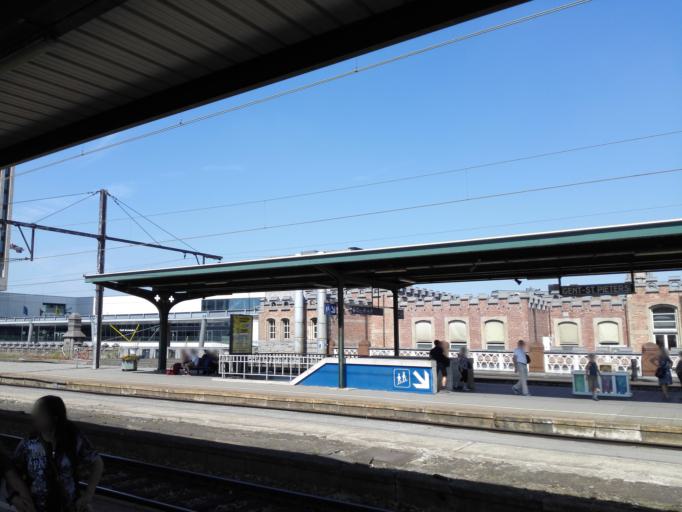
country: BE
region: Flanders
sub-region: Provincie Oost-Vlaanderen
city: Gent
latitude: 51.0356
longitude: 3.7101
